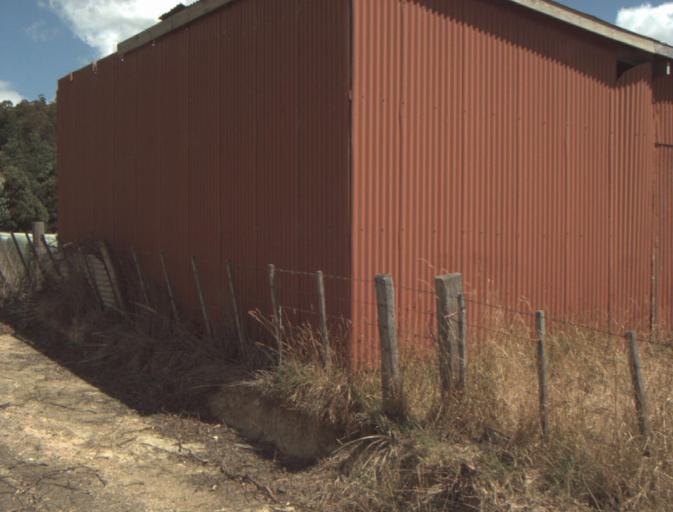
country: AU
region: Tasmania
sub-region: Launceston
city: Mayfield
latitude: -41.2349
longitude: 147.1256
